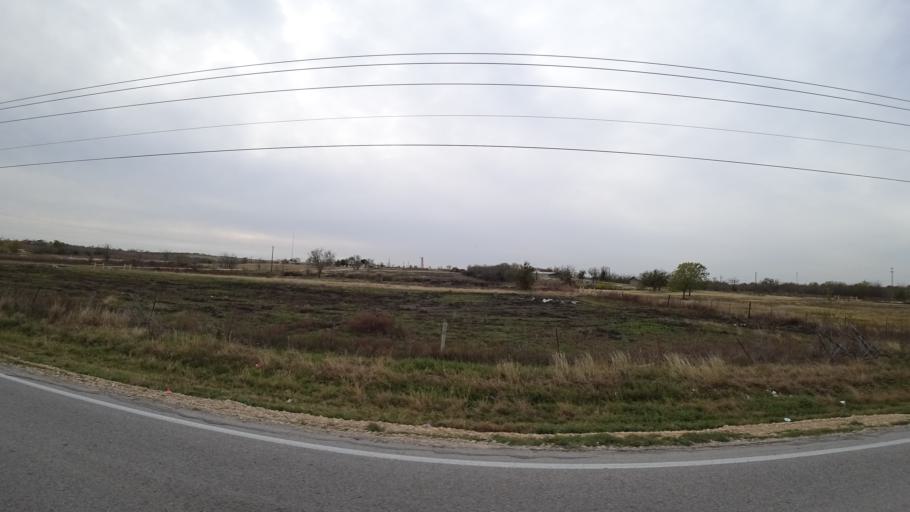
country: US
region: Texas
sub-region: Travis County
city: Garfield
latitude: 30.1498
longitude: -97.6310
